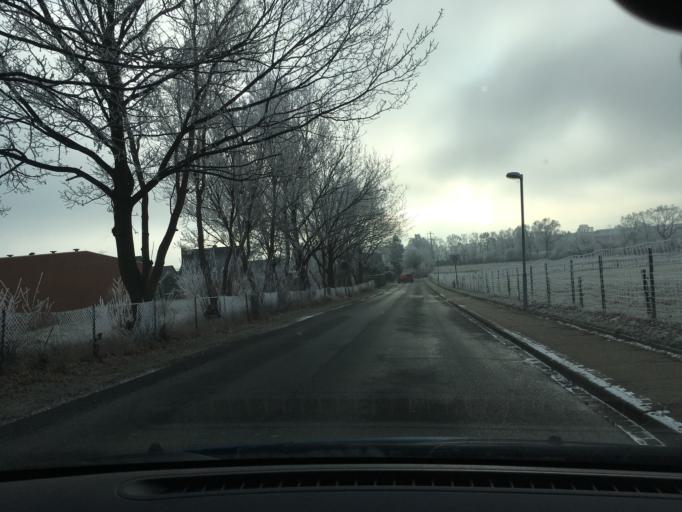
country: DE
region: Lower Saxony
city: Bardowick
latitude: 53.2725
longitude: 10.4001
